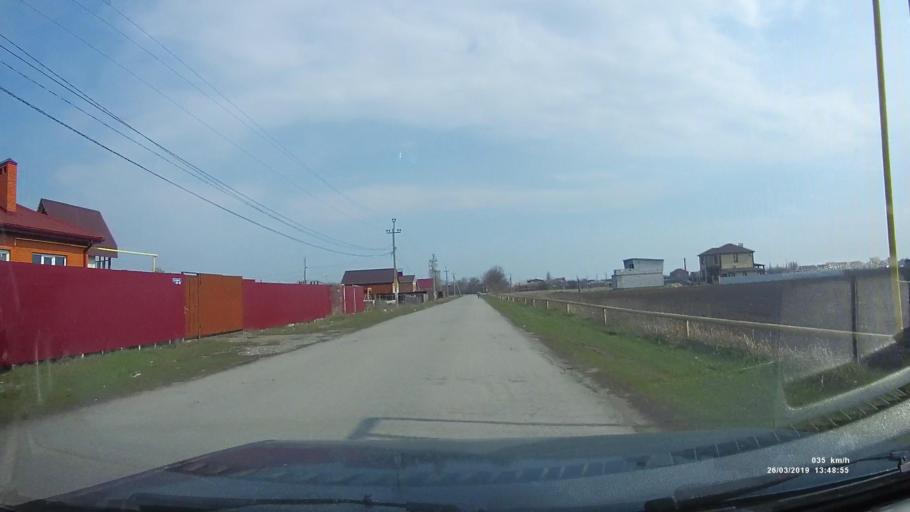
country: RU
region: Rostov
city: Novobessergenovka
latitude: 47.1915
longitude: 38.8621
